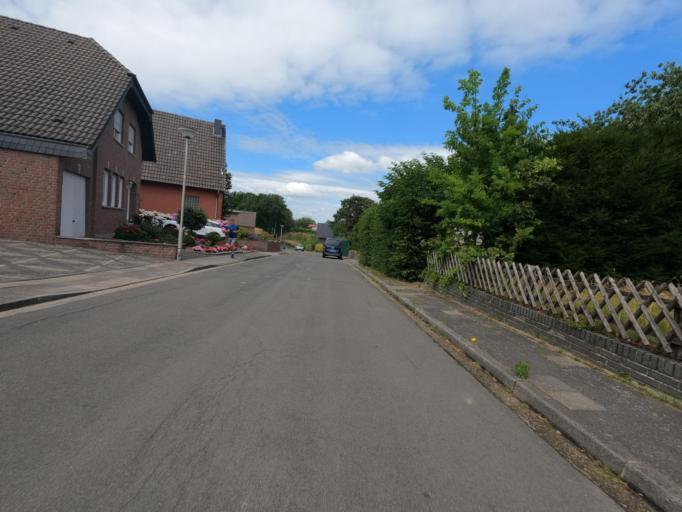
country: DE
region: North Rhine-Westphalia
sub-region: Regierungsbezirk Koln
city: Heinsberg
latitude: 51.0517
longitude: 6.1115
